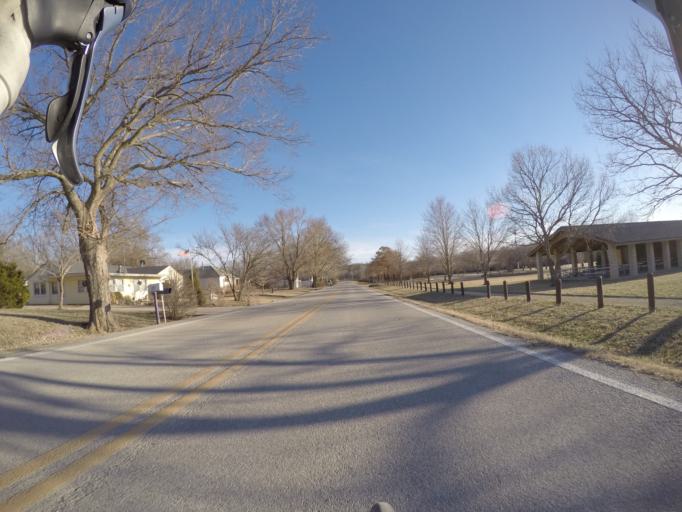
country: US
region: Kansas
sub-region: Riley County
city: Ogden
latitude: 39.2242
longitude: -96.7101
